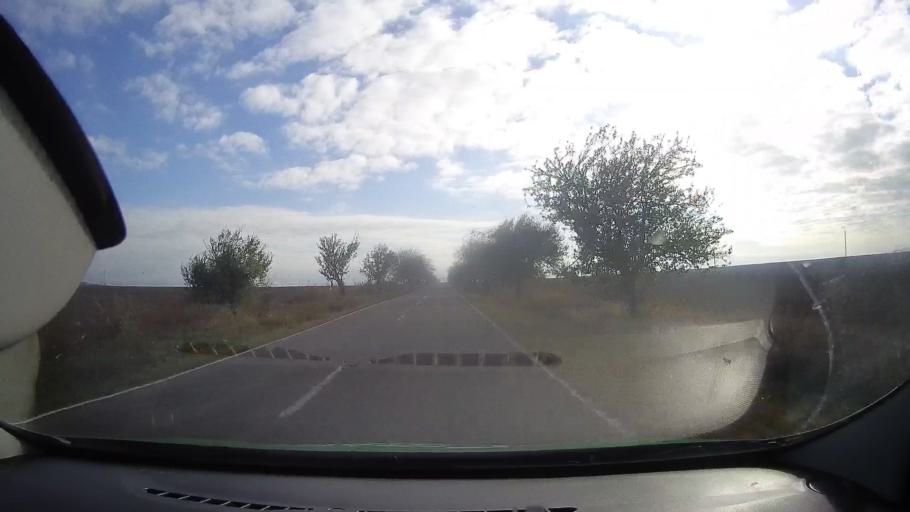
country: RO
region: Tulcea
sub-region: Comuna Bestepe
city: Bestepe
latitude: 45.0796
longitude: 29.0383
